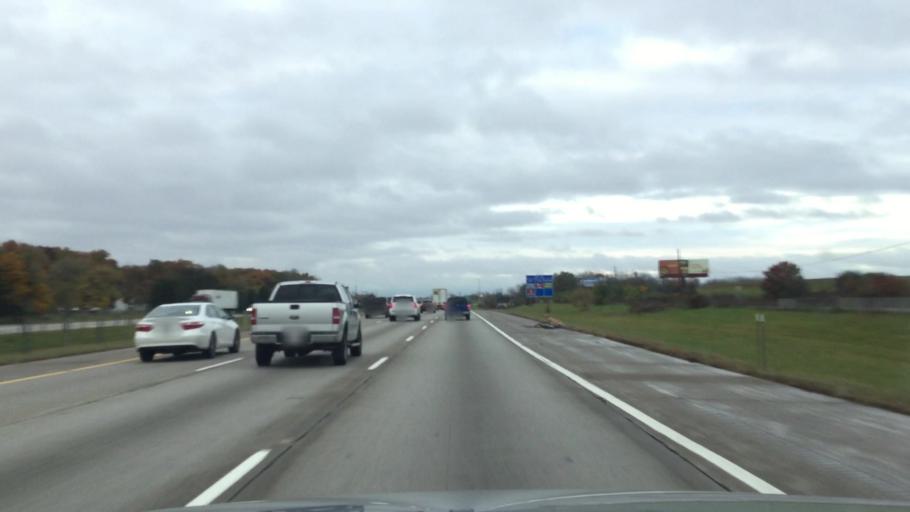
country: US
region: Michigan
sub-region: Wayne County
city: Belleville
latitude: 42.2191
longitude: -83.5289
